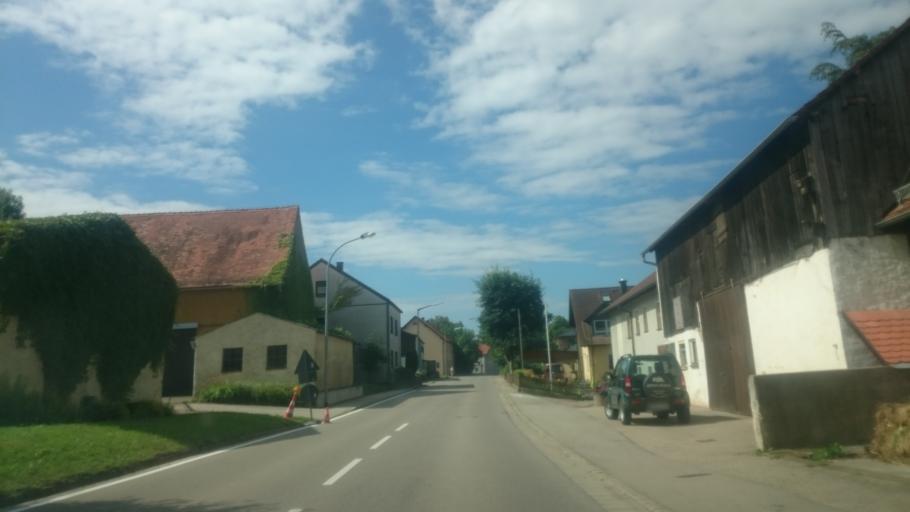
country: DE
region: Bavaria
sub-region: Regierungsbezirk Mittelfranken
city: Ettenstatt
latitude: 49.0325
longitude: 11.0501
